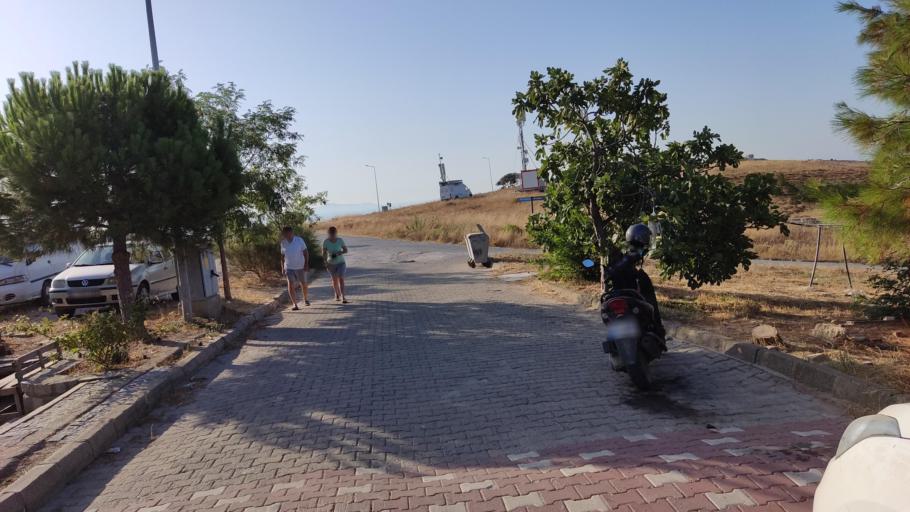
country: TR
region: Canakkale
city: Bozcaada
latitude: 39.8314
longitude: 26.0697
